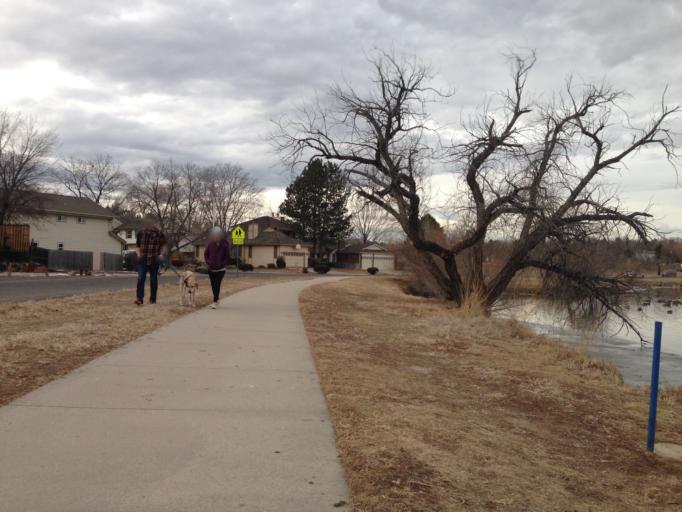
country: US
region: Colorado
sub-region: Adams County
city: Westminster
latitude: 39.8429
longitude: -105.0700
